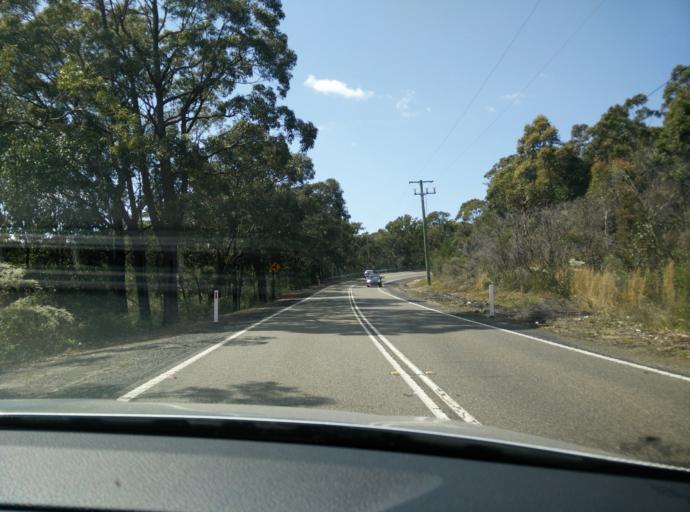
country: AU
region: New South Wales
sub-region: Gosford Shire
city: Blackwall
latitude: -33.4845
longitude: 151.3034
